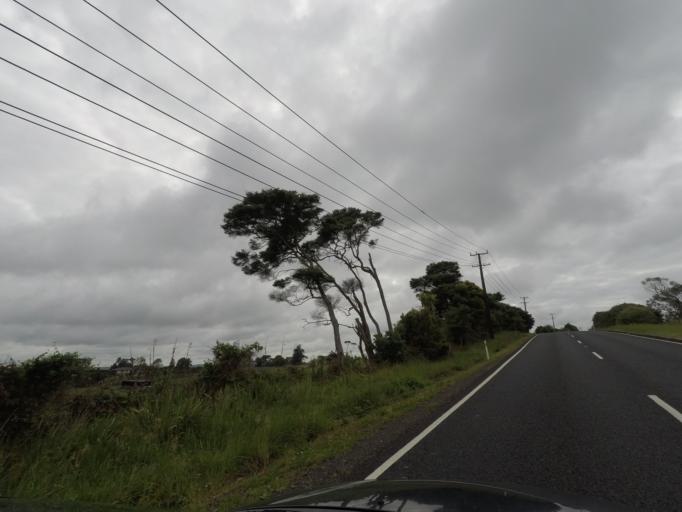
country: NZ
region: Auckland
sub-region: Auckland
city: Rosebank
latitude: -36.8217
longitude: 174.5732
